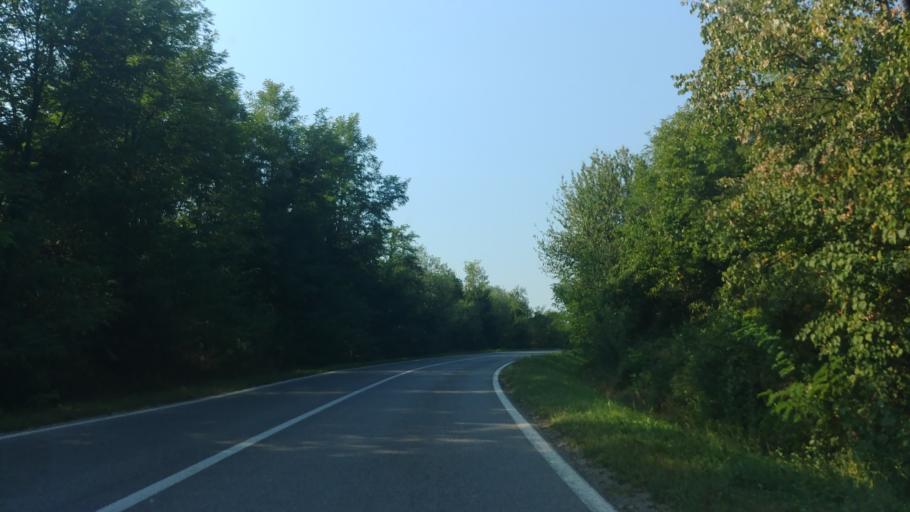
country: BA
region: Brcko
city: Brcko
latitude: 44.7701
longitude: 18.8099
